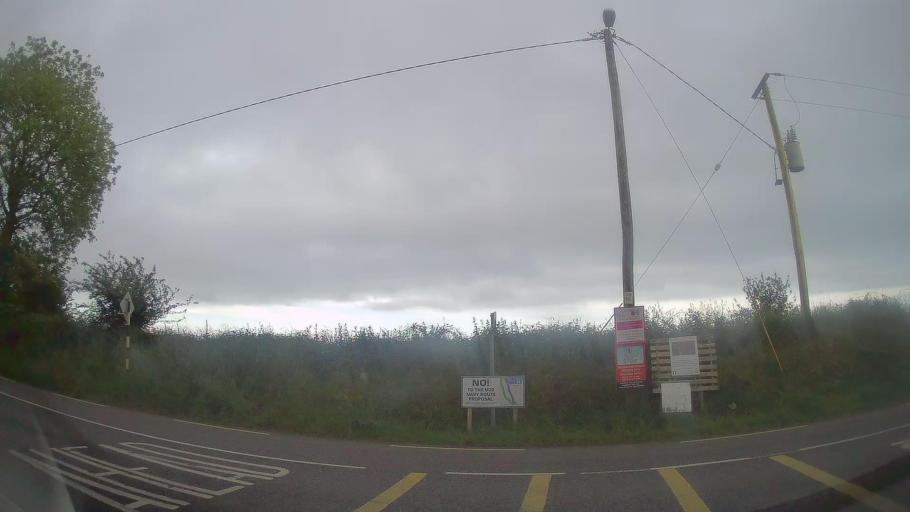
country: IE
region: Munster
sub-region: County Cork
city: Blarney
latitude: 51.9803
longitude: -8.5328
